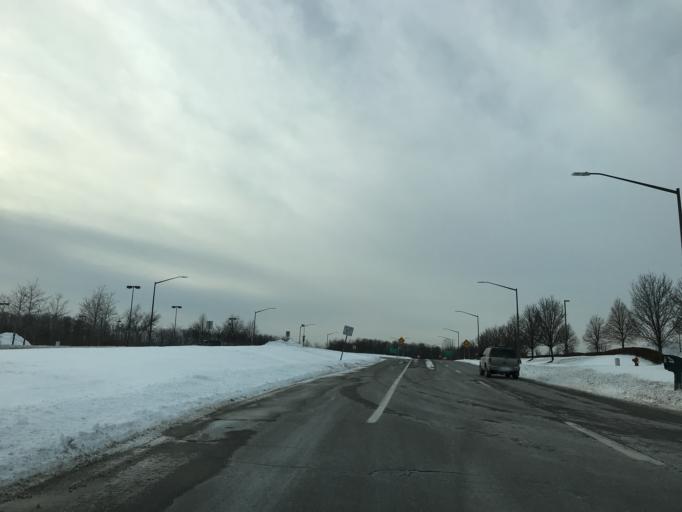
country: US
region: Michigan
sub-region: Oakland County
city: Wolverine Lake
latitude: 42.5352
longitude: -83.4440
